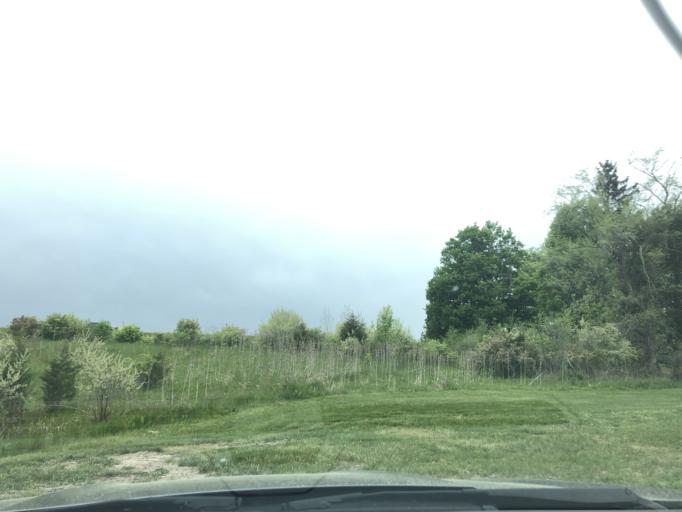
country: US
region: Michigan
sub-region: Eaton County
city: Dimondale
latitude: 42.6712
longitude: -84.6806
